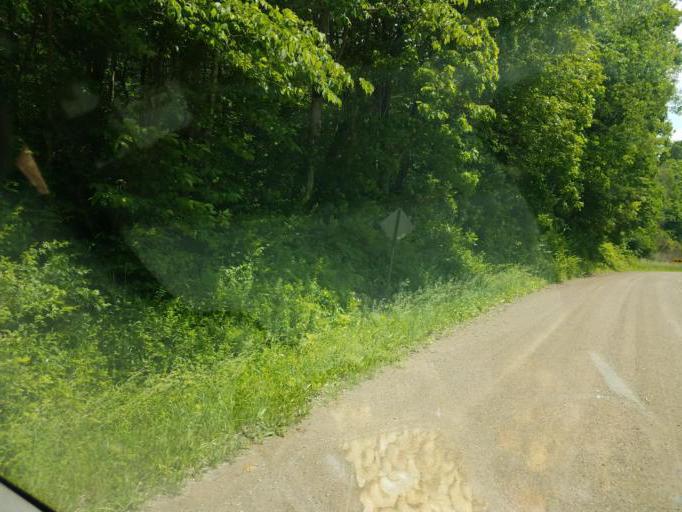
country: US
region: Ohio
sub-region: Knox County
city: Oak Hill
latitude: 40.3454
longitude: -82.2410
